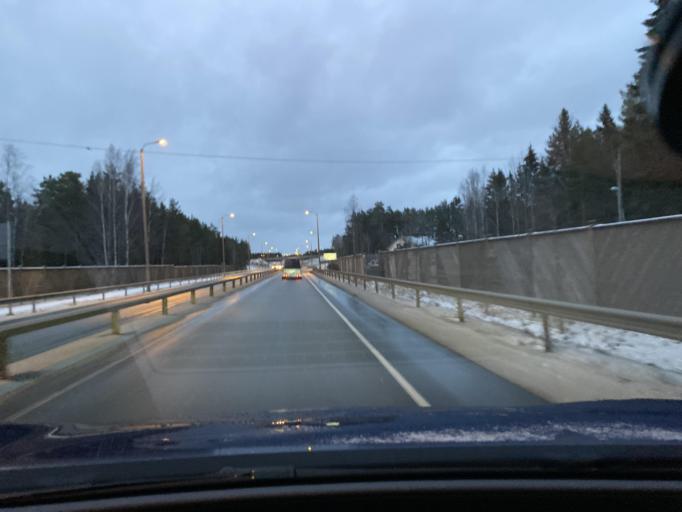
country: FI
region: Satakunta
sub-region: Rauma
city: Rauma
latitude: 61.1469
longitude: 21.5604
